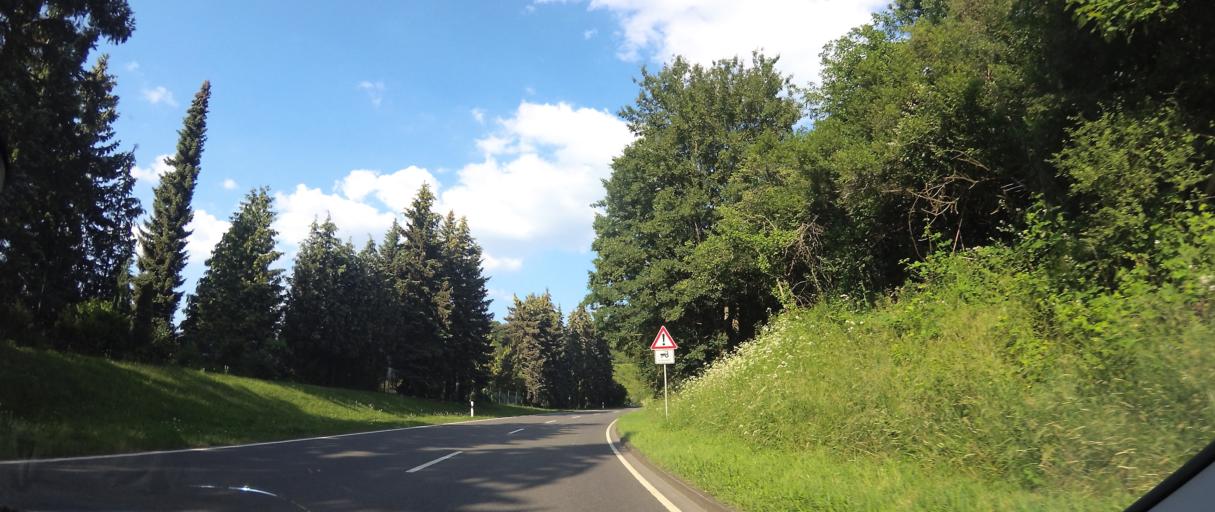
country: DE
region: Rheinland-Pfalz
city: Hochstatten
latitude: 49.7615
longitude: 7.8322
